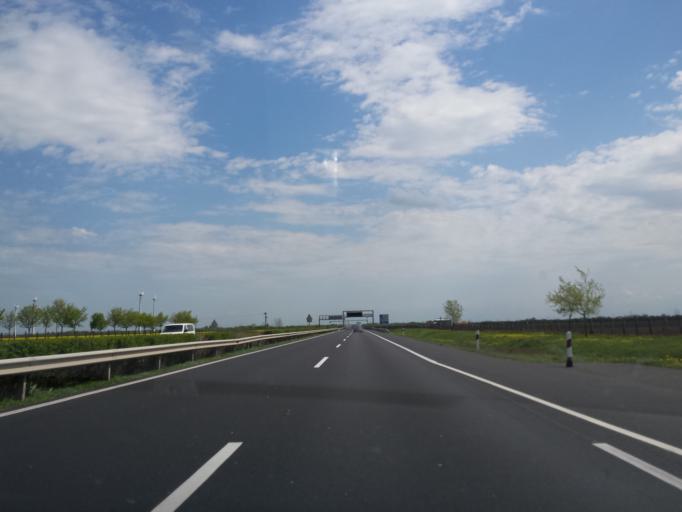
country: HU
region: Gyor-Moson-Sopron
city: Mosonmagyarovar
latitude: 47.8812
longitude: 17.1971
